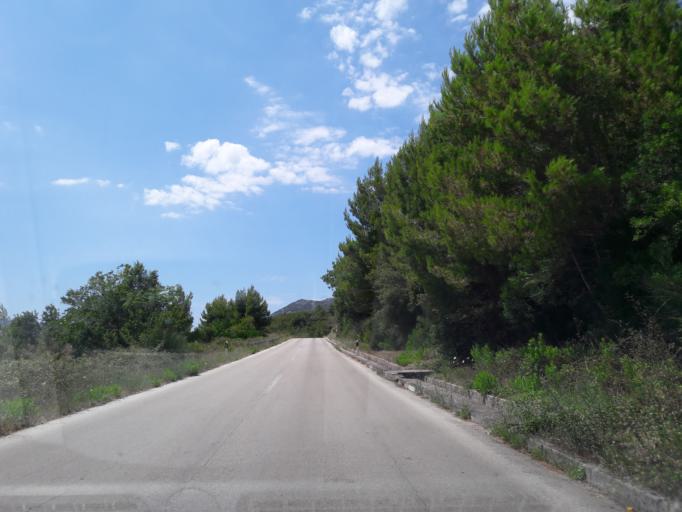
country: HR
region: Dubrovacko-Neretvanska
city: Korcula
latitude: 42.9822
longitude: 17.1166
